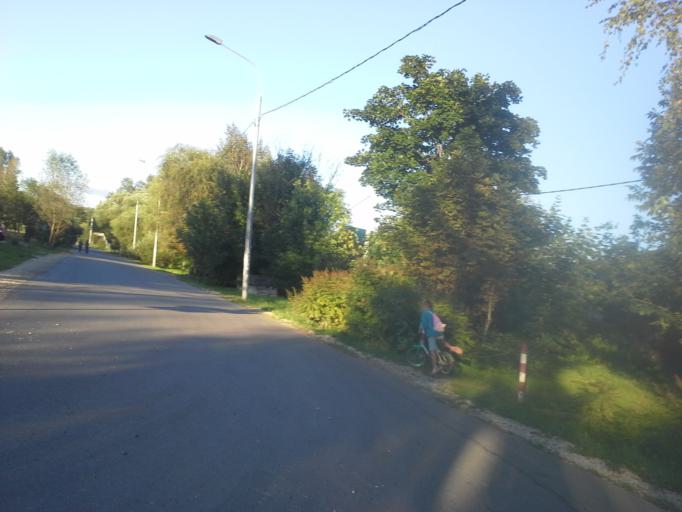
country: RU
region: Moskovskaya
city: Kievskij
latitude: 55.4624
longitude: 36.8861
